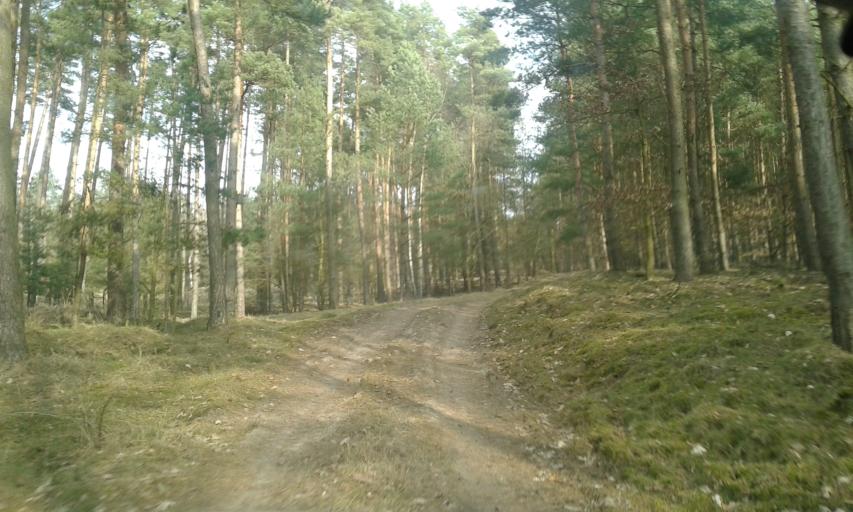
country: PL
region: West Pomeranian Voivodeship
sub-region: Powiat mysliborski
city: Barlinek
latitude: 53.0864
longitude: 15.2148
